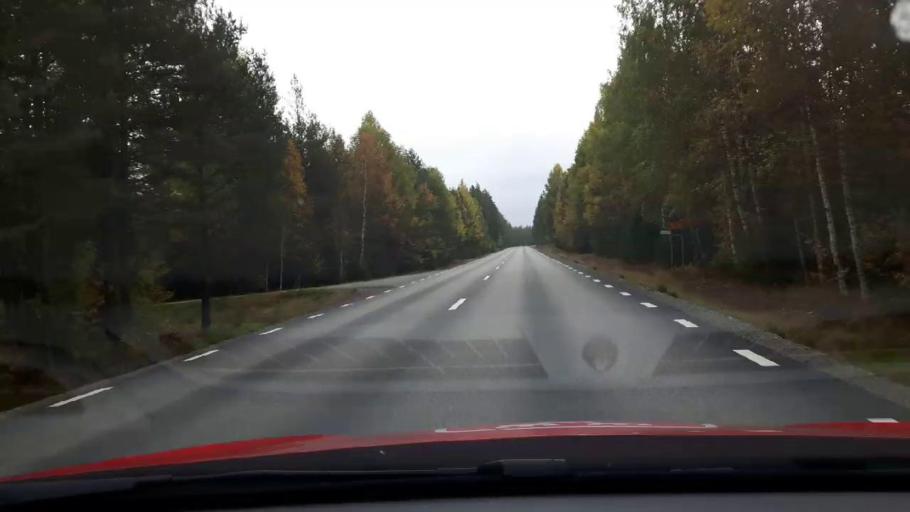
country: SE
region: Gaevleborg
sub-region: Ljusdals Kommun
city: Farila
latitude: 61.8560
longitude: 15.7464
